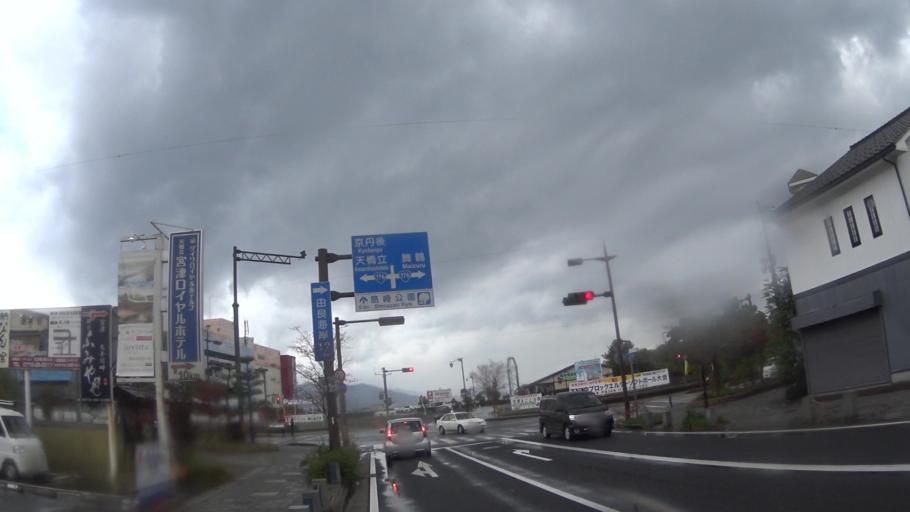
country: JP
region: Kyoto
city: Miyazu
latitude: 35.5373
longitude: 135.1933
